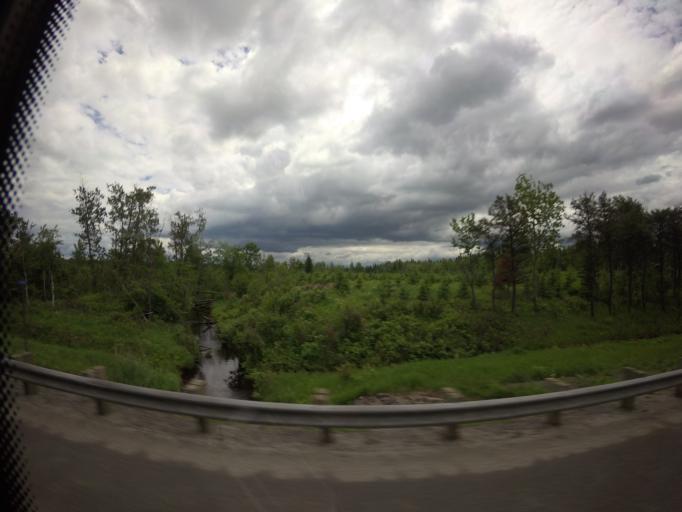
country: CA
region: Quebec
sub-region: Capitale-Nationale
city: Cap-Sante
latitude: 46.4677
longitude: -71.7307
